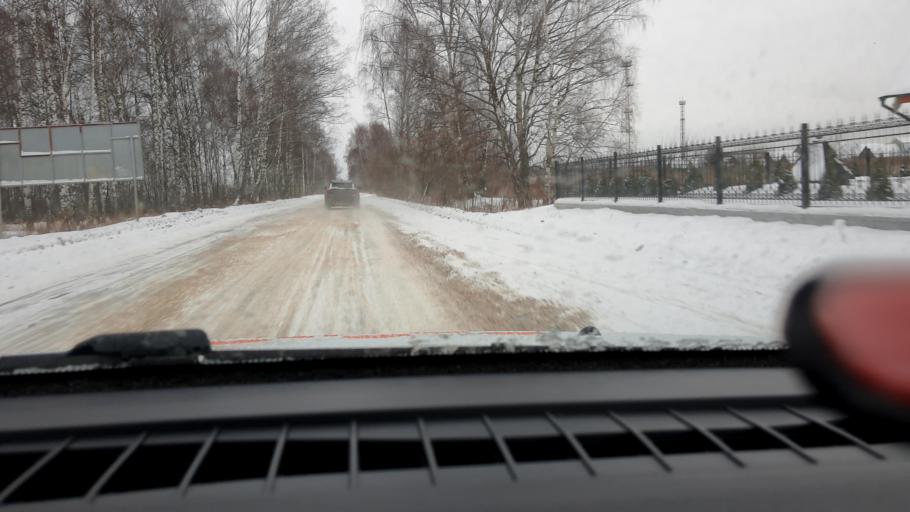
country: RU
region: Nizjnij Novgorod
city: Pamyat' Parizhskoy Kommuny
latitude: 56.2687
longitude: 44.4245
